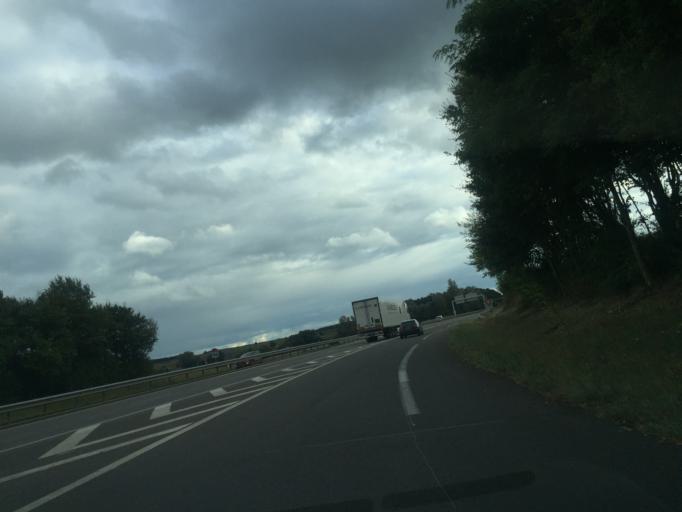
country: FR
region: Lorraine
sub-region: Departement des Vosges
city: Chatenois
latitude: 48.3002
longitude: 5.8573
